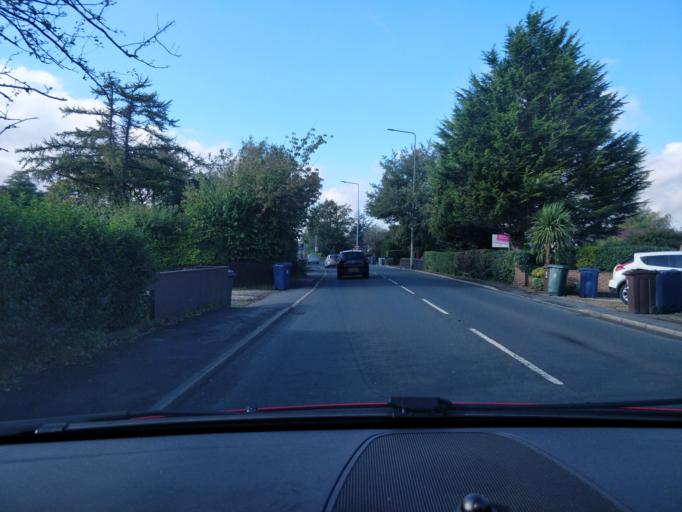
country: GB
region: England
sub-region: Sefton
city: Southport
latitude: 53.6196
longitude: -2.9518
